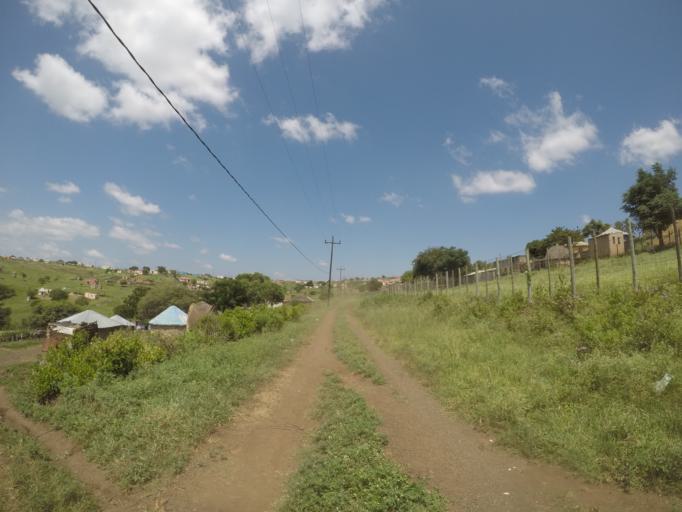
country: ZA
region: KwaZulu-Natal
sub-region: uThungulu District Municipality
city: Empangeni
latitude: -28.6057
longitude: 31.7351
